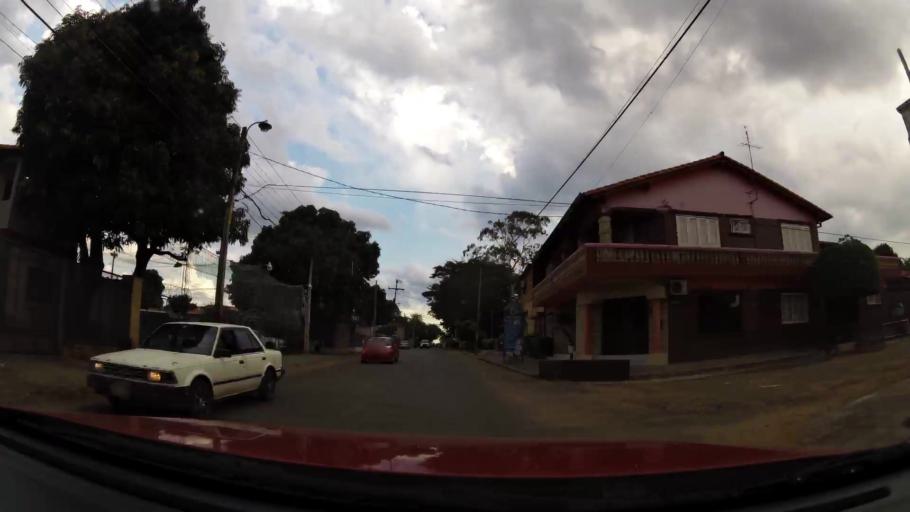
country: PY
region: Central
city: Fernando de la Mora
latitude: -25.3420
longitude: -57.5586
